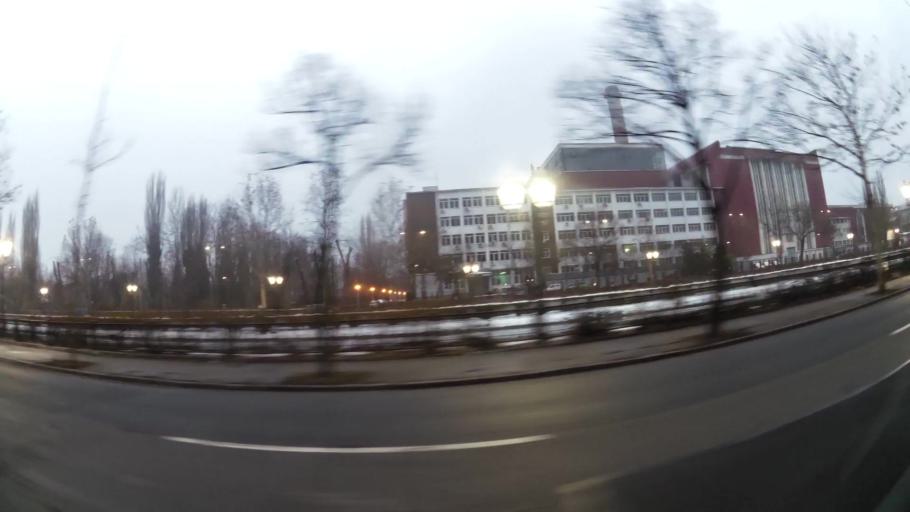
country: RO
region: Bucuresti
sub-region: Municipiul Bucuresti
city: Bucuresti
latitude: 44.4411
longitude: 26.0657
